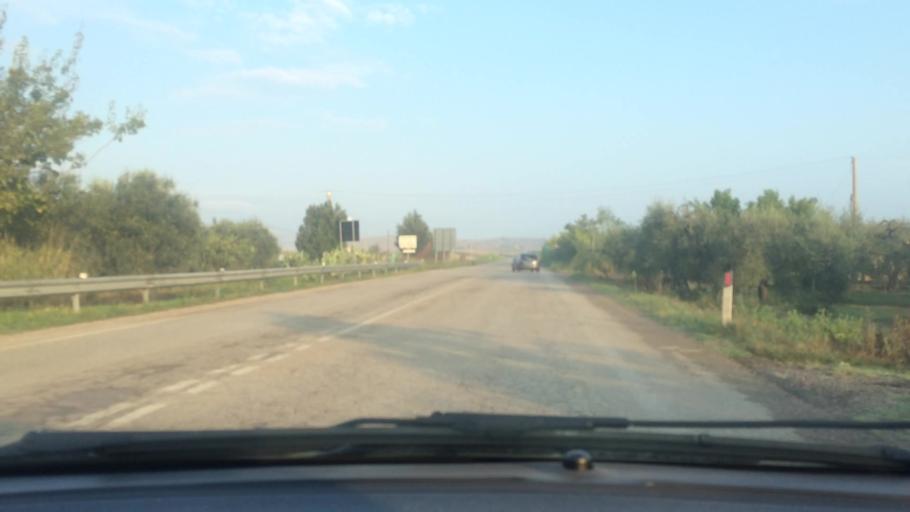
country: IT
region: Basilicate
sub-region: Provincia di Matera
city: Montescaglioso
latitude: 40.5272
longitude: 16.6248
